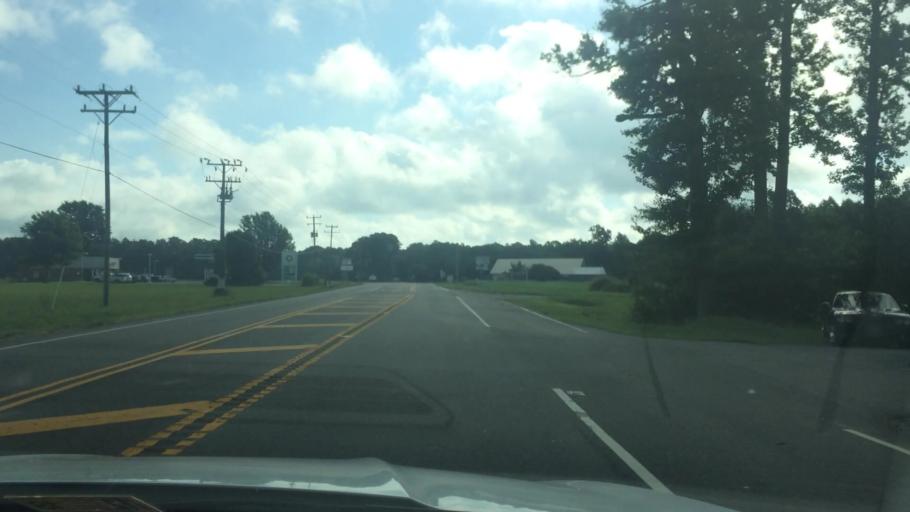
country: US
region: Virginia
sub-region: Middlesex County
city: Deltaville
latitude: 37.4949
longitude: -76.4132
